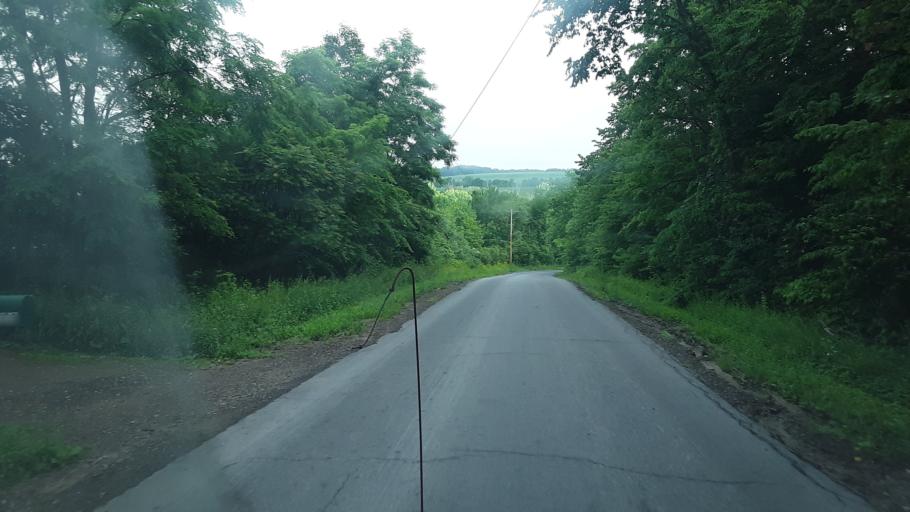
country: US
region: New York
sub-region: Montgomery County
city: Fonda
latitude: 42.8764
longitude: -74.3773
